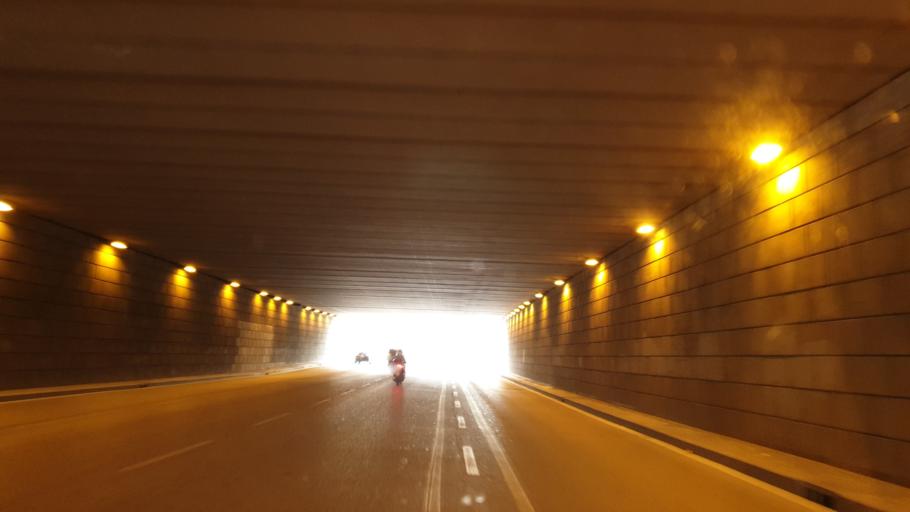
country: IT
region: Tuscany
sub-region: Province of Florence
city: Florence
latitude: 43.7803
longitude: 11.2492
